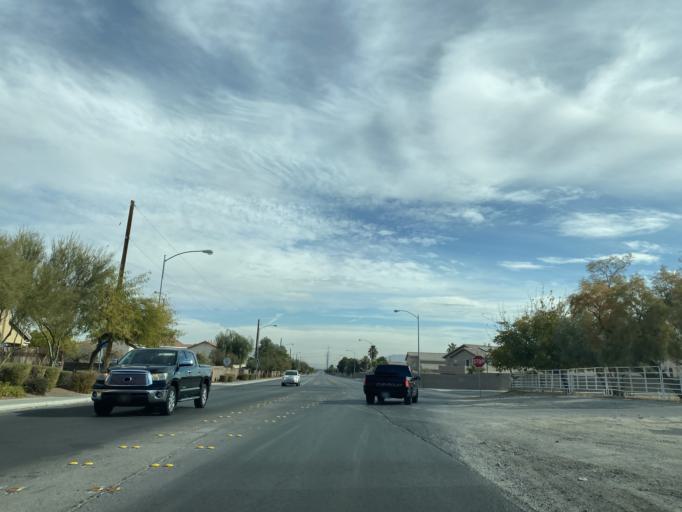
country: US
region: Nevada
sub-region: Clark County
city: North Las Vegas
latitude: 36.2469
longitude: -115.1310
